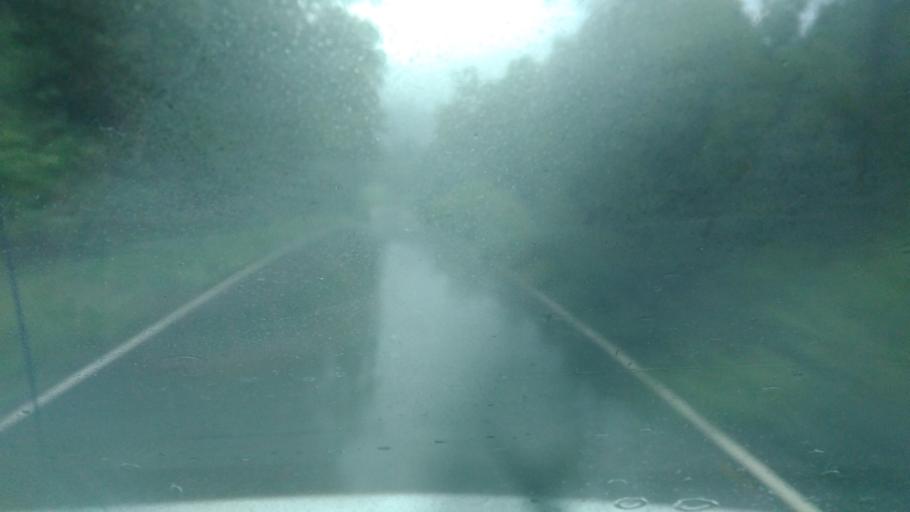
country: US
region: Kentucky
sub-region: Lewis County
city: Vanceburg
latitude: 38.5154
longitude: -83.4794
